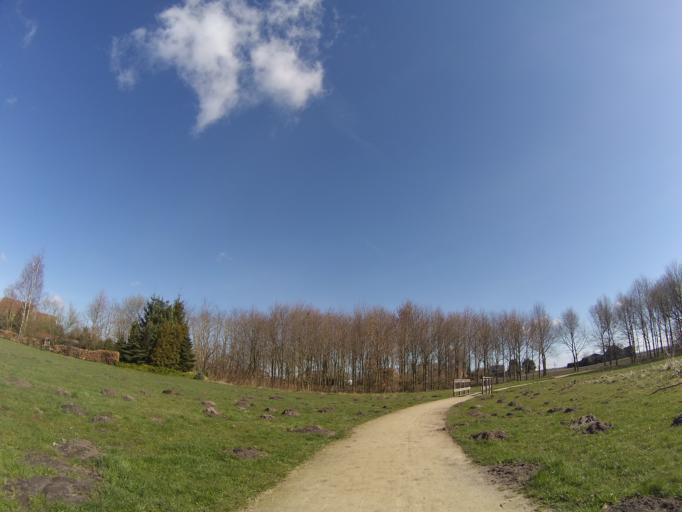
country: NL
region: Drenthe
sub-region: Gemeente Emmen
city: Emmen
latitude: 52.7315
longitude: 6.9178
